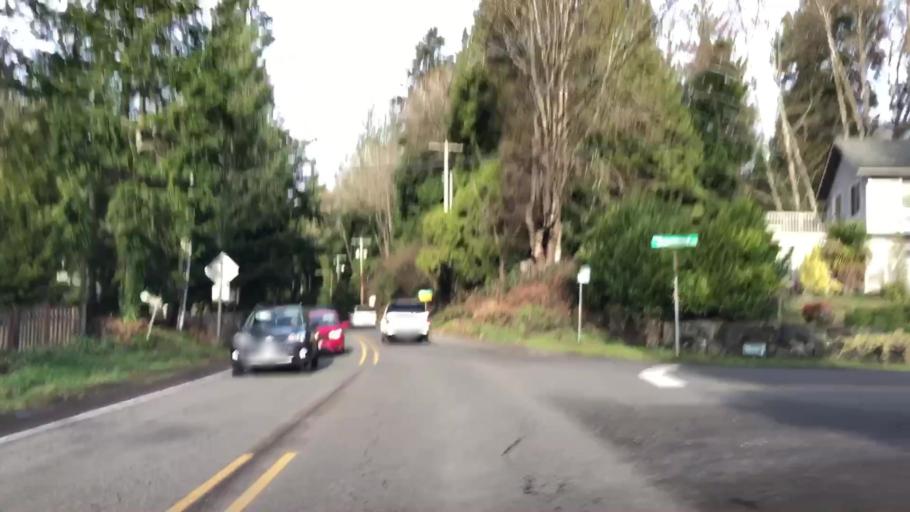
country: US
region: Washington
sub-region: Kitsap County
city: Indianola
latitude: 47.7615
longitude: -122.5510
